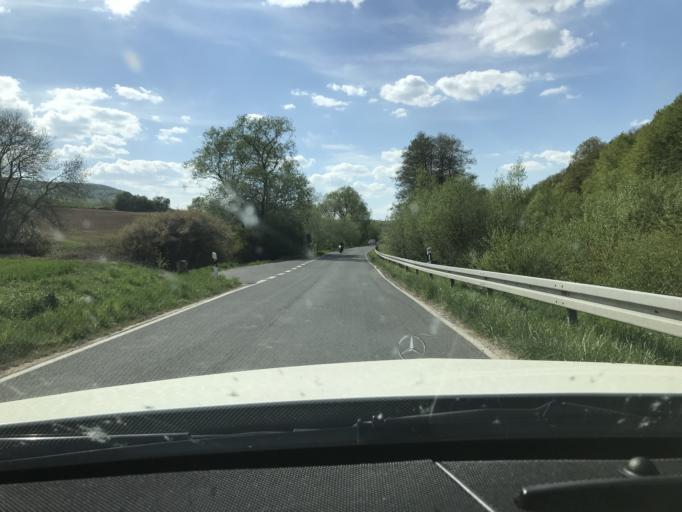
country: DE
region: Hesse
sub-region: Regierungsbezirk Kassel
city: Weissenborn
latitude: 51.1278
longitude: 10.1365
